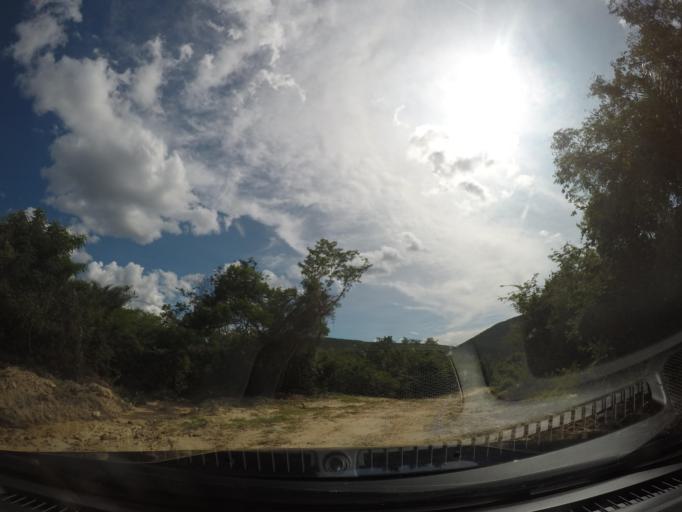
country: BR
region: Bahia
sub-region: Barra Da Estiva
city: Barra da Estiva
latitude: -13.1428
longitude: -41.5930
